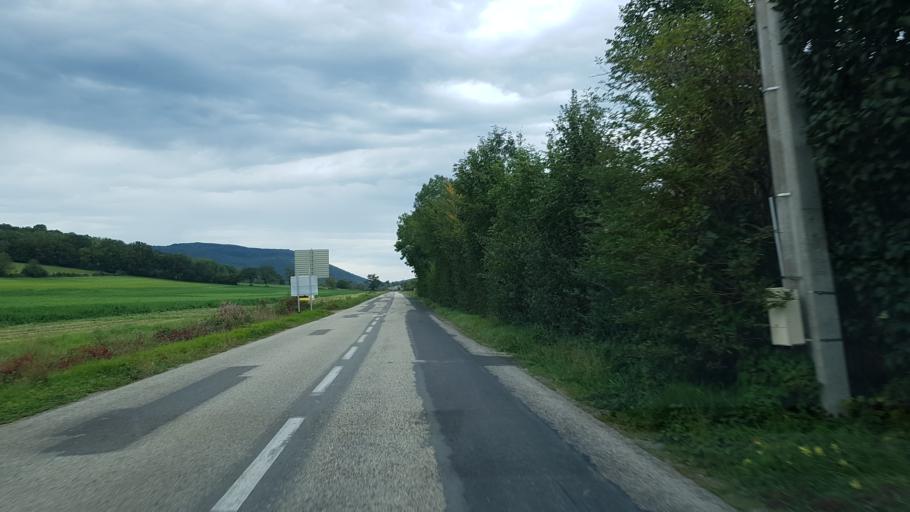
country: FR
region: Rhone-Alpes
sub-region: Departement de l'Ain
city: Cuisiat
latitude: 46.2478
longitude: 5.4234
